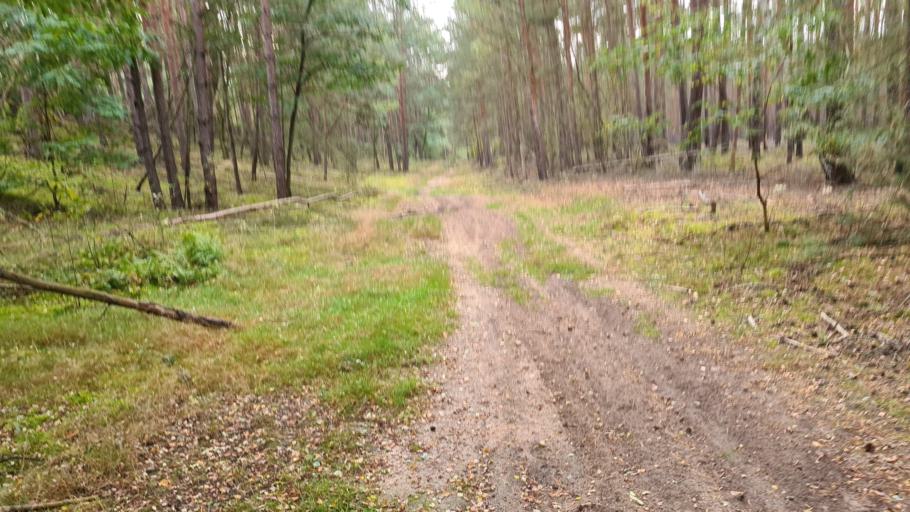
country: DE
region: Brandenburg
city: Schonewalde
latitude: 51.6299
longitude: 13.6139
